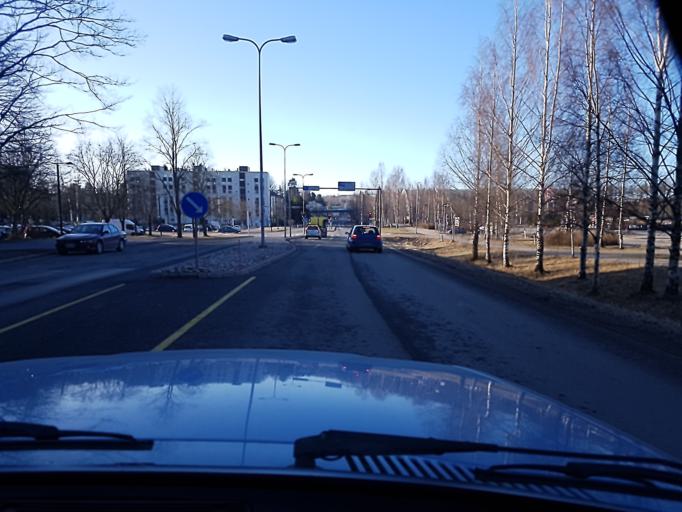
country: FI
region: Uusimaa
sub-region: Helsinki
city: Teekkarikylae
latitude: 60.2645
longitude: 24.8428
